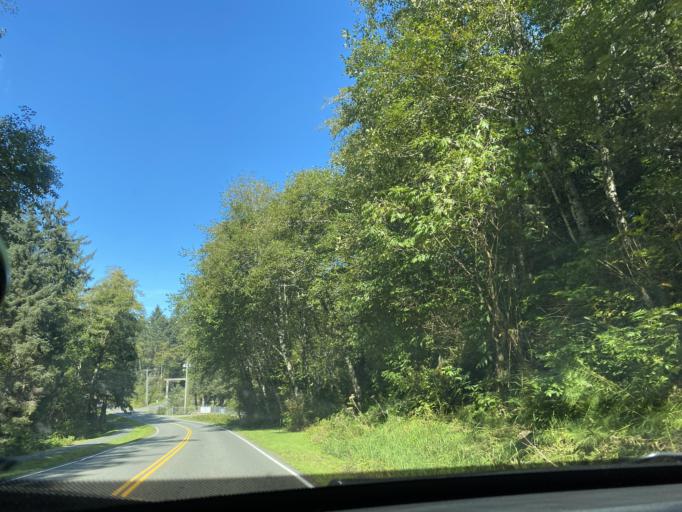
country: US
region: Washington
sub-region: Clallam County
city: Forks
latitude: 47.9011
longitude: -124.6268
